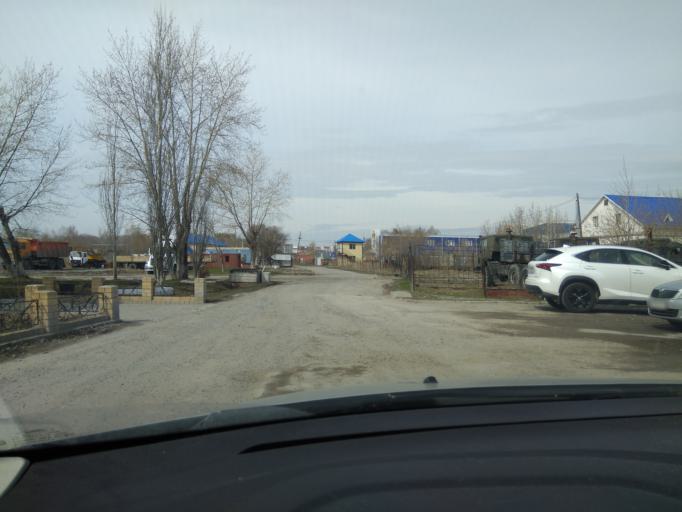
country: RU
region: Tjumen
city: Melioratorov
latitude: 57.1905
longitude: 65.5976
